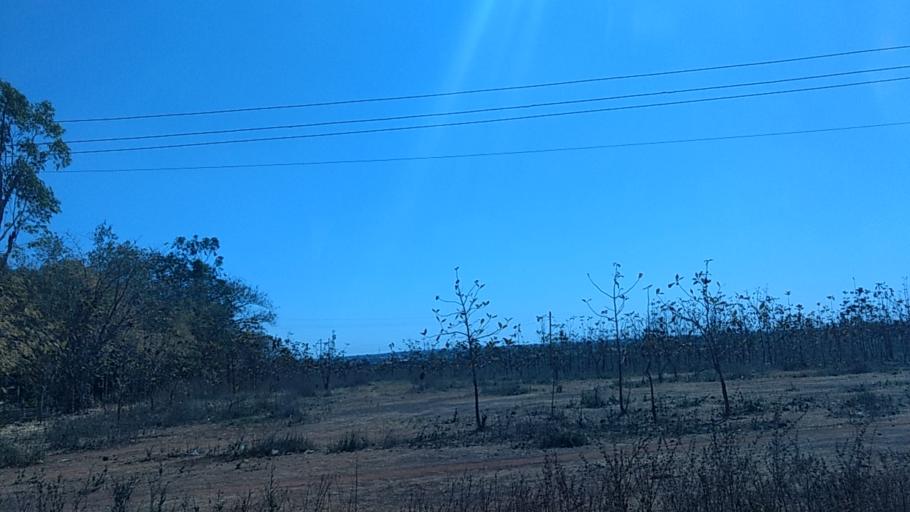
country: IN
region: Maharashtra
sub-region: Bhandara
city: Pauni
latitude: 20.6203
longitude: 79.8478
